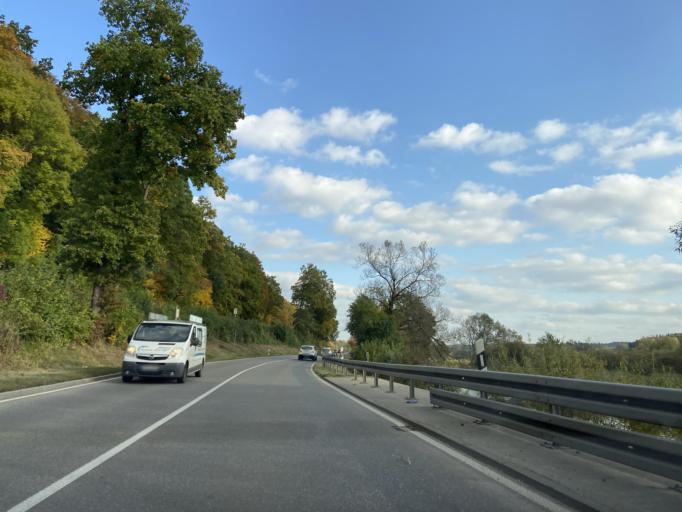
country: DE
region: Baden-Wuerttemberg
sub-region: Tuebingen Region
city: Sigmaringen
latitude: 48.0770
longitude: 9.2399
